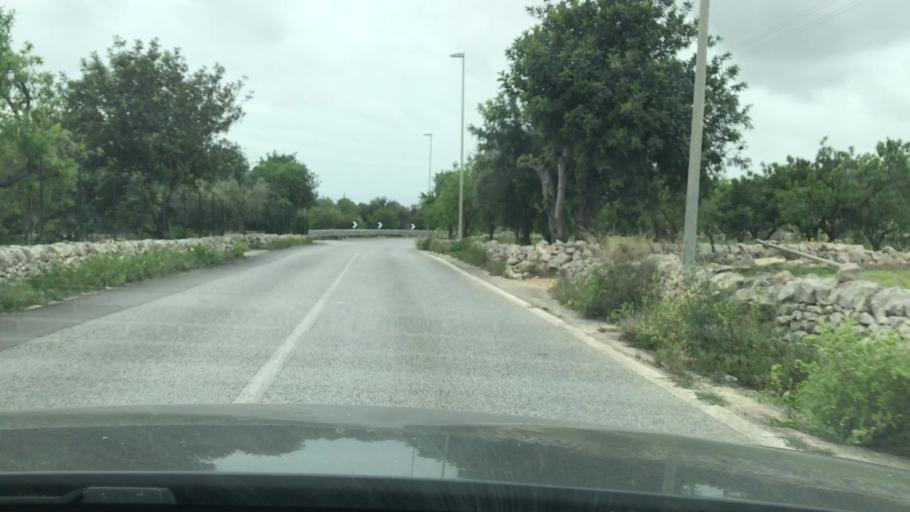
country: IT
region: Sicily
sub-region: Ragusa
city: Scicli
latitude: 36.8010
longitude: 14.7166
